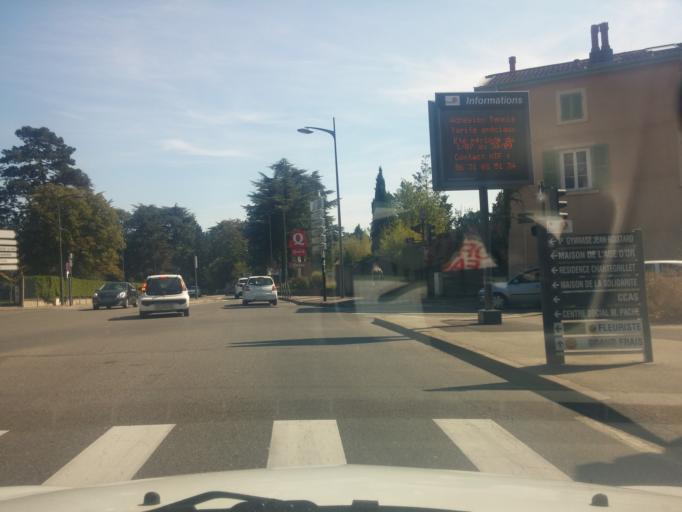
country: FR
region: Rhone-Alpes
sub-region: Departement du Rhone
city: Francheville
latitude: 45.7384
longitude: 4.7733
